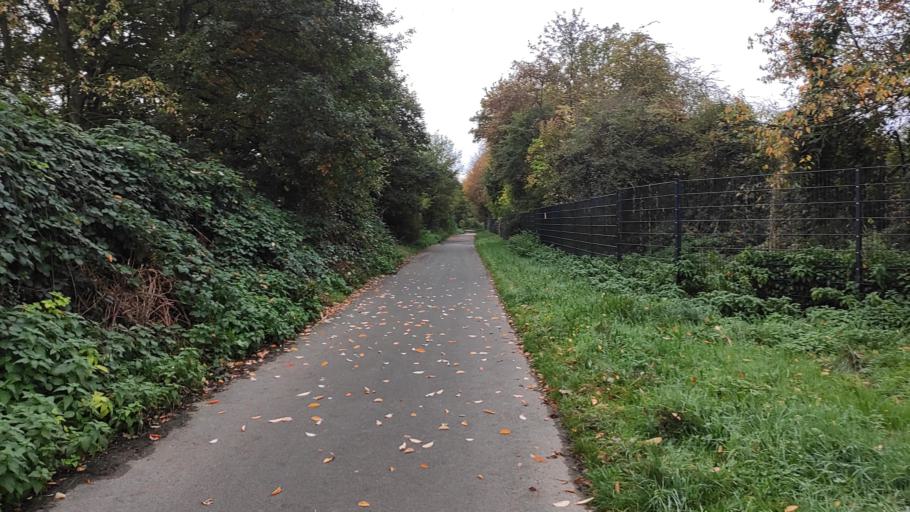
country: DE
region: North Rhine-Westphalia
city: Sprockhovel
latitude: 51.4169
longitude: 7.2676
